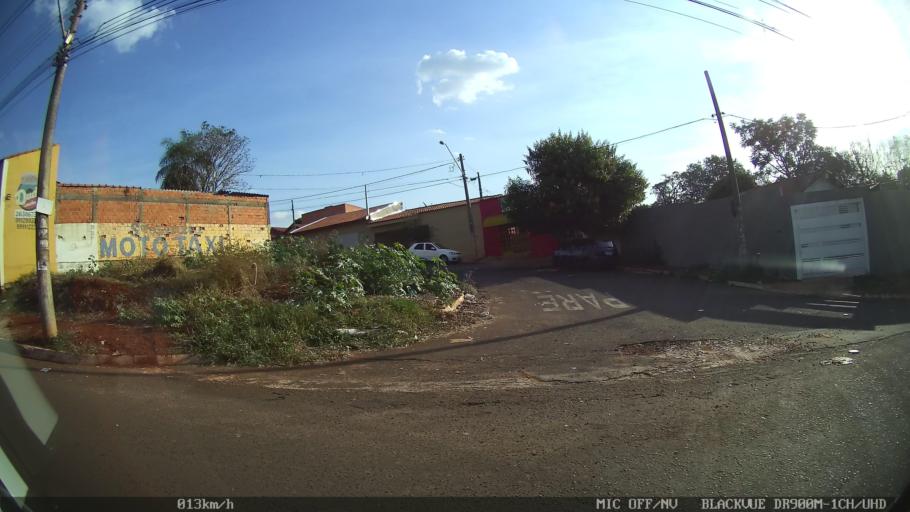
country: BR
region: Sao Paulo
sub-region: Ribeirao Preto
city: Ribeirao Preto
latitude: -21.1533
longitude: -47.8420
